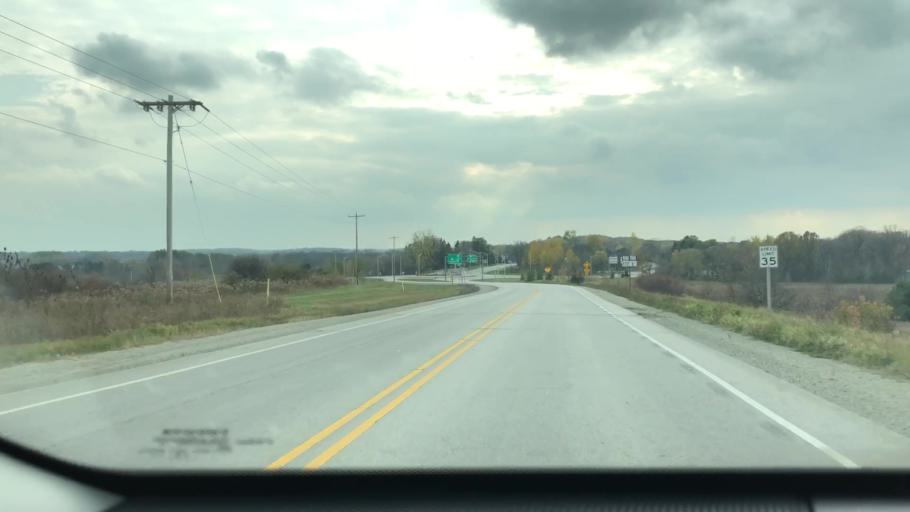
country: US
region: Wisconsin
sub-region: Brown County
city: Oneida
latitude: 44.5030
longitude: -88.1743
